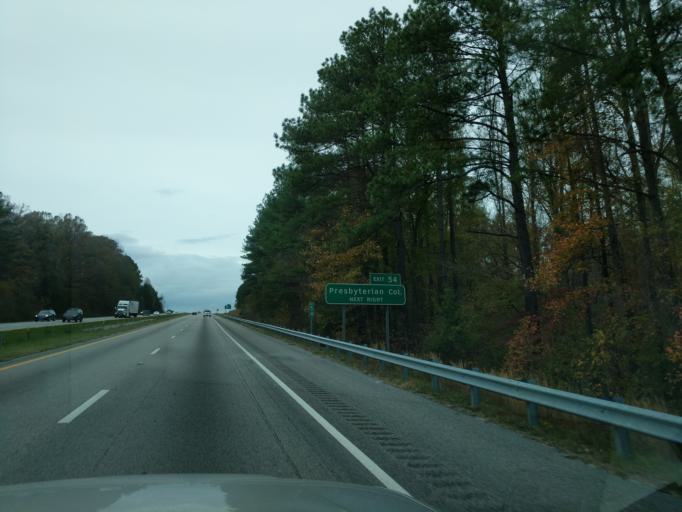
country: US
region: South Carolina
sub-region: Laurens County
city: Clinton
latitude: 34.4920
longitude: -81.8386
